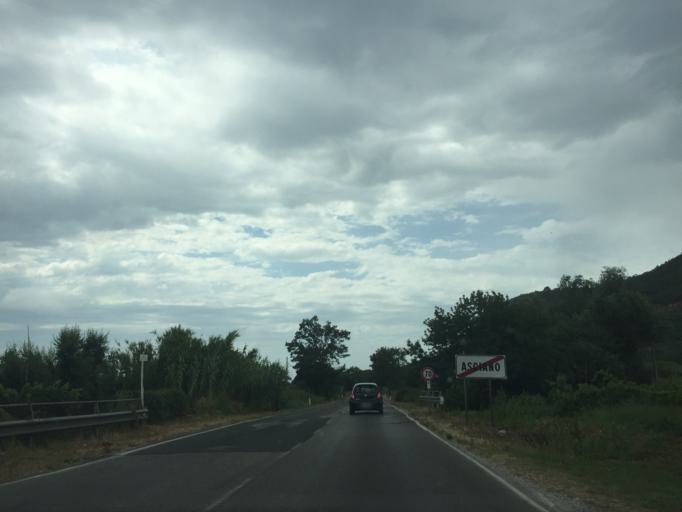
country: IT
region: Tuscany
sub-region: Province of Pisa
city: Asciano
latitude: 43.7489
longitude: 10.4597
